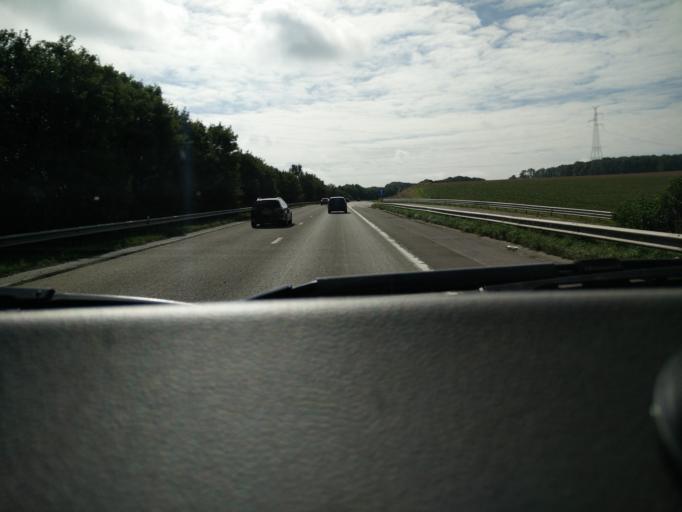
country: BE
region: Wallonia
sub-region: Province de Namur
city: Ciney
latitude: 50.2580
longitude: 5.0450
